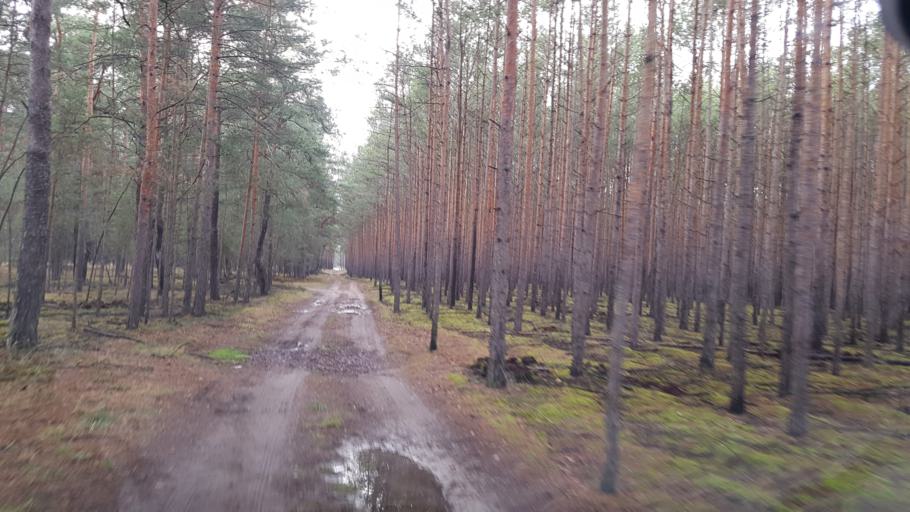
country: DE
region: Brandenburg
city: Sallgast
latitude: 51.6310
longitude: 13.8305
